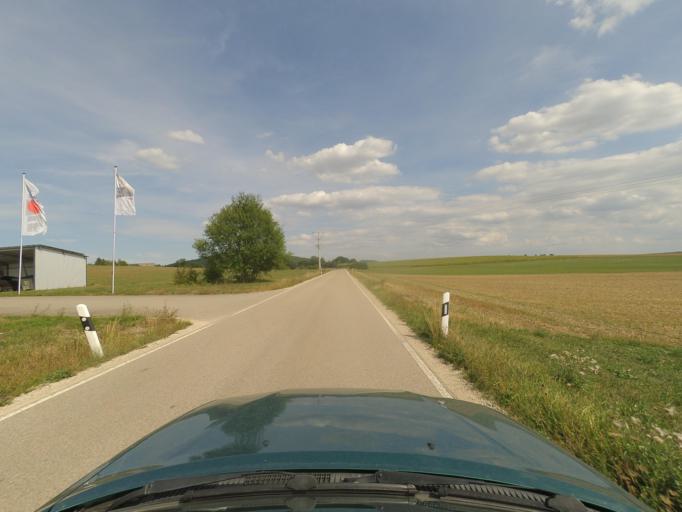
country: DE
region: Bavaria
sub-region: Upper Palatinate
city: Freystadt
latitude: 49.1724
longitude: 11.3650
